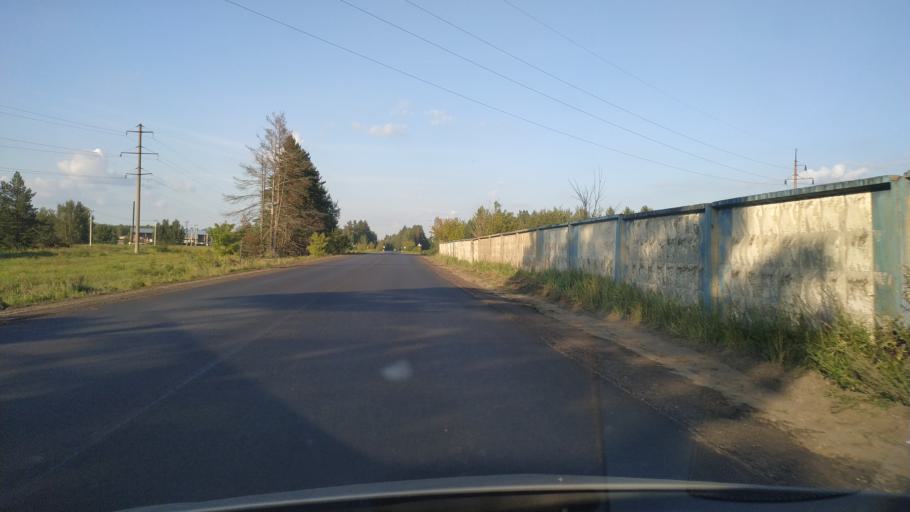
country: RU
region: Moskovskaya
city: Kerva
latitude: 55.5768
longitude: 39.6846
